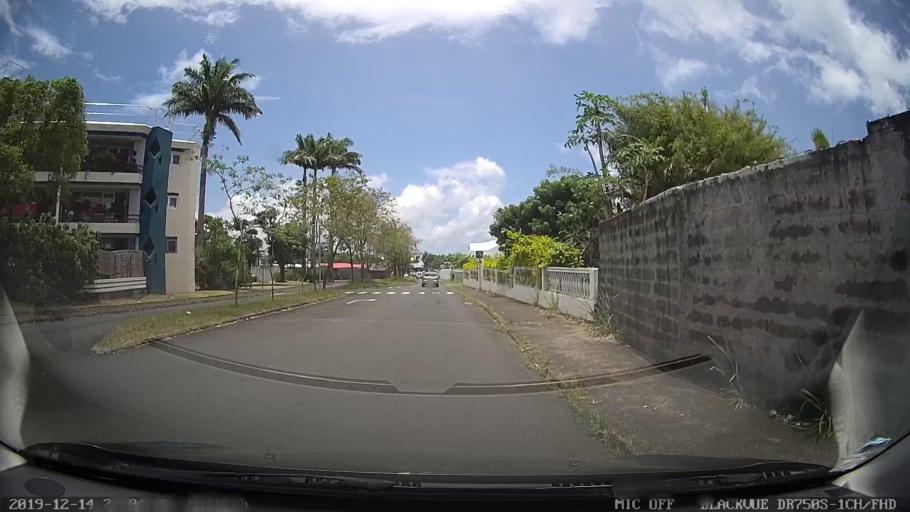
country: RE
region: Reunion
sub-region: Reunion
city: Saint-Andre
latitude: -20.9572
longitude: 55.6549
